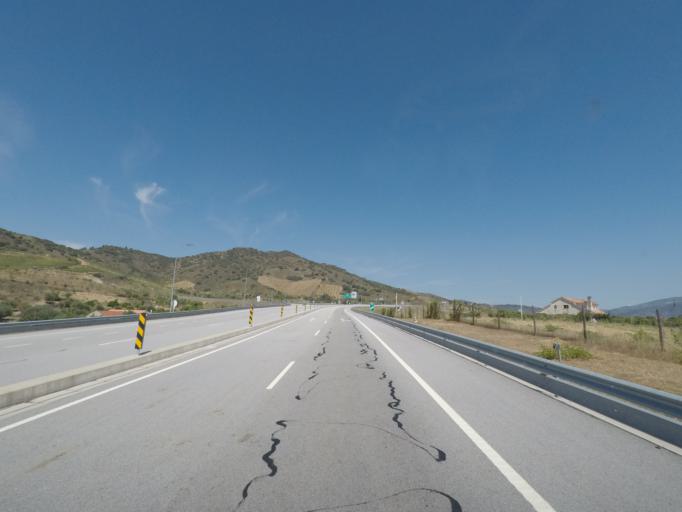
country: PT
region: Braganca
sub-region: Braganca Municipality
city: Vila Flor
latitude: 41.3210
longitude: -7.0789
